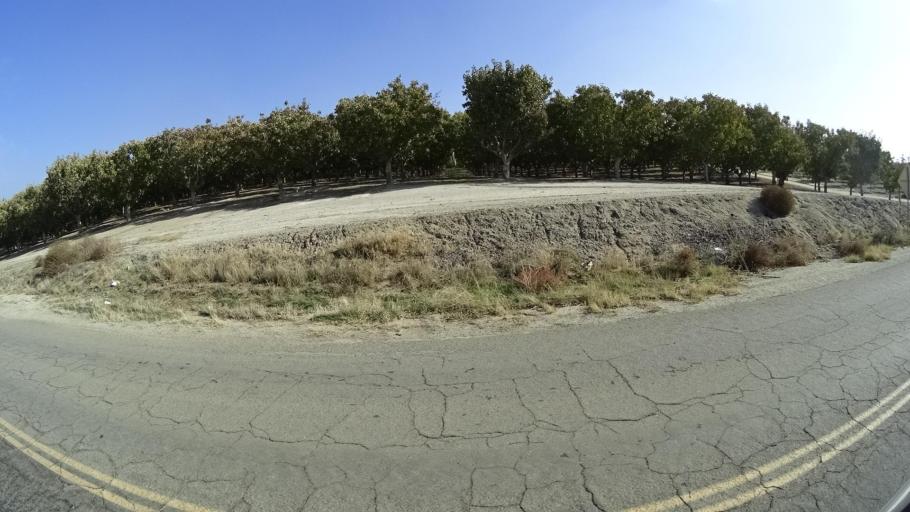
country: US
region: California
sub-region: Kern County
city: McFarland
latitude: 35.6463
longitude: -119.1336
